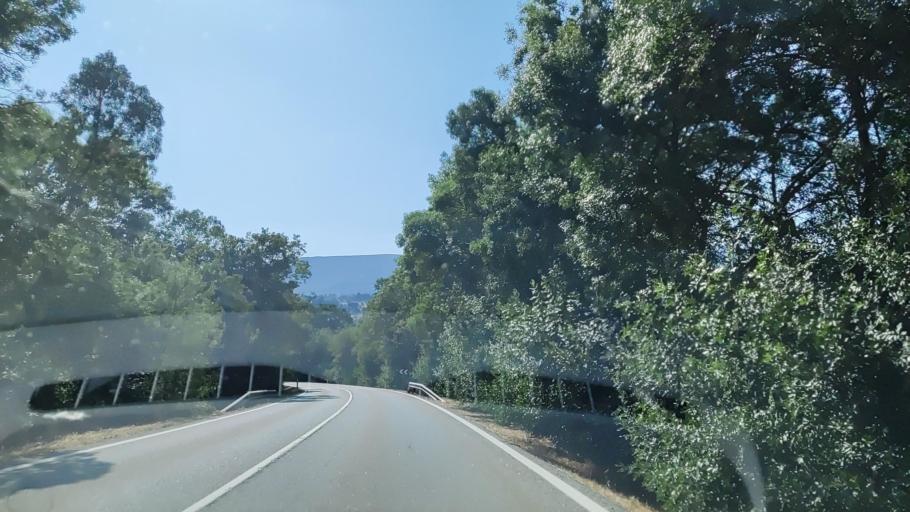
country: ES
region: Madrid
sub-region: Provincia de Madrid
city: Lozoya
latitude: 40.9561
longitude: -3.7797
